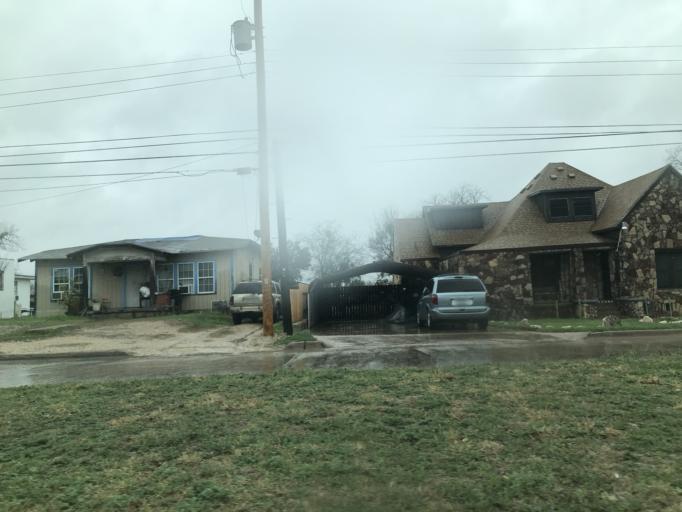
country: US
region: Texas
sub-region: Tom Green County
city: San Angelo
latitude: 31.4653
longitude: -100.4297
